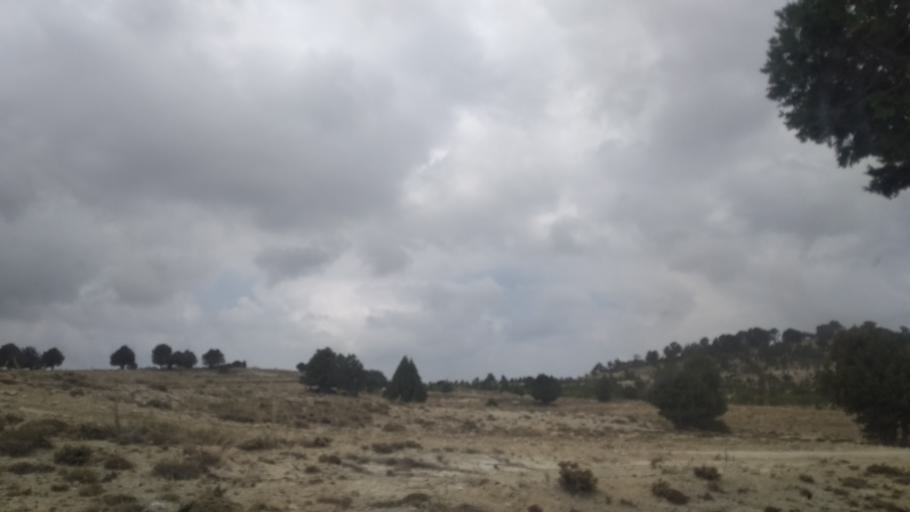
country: TR
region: Mersin
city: Sarikavak
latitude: 36.5756
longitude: 33.7573
